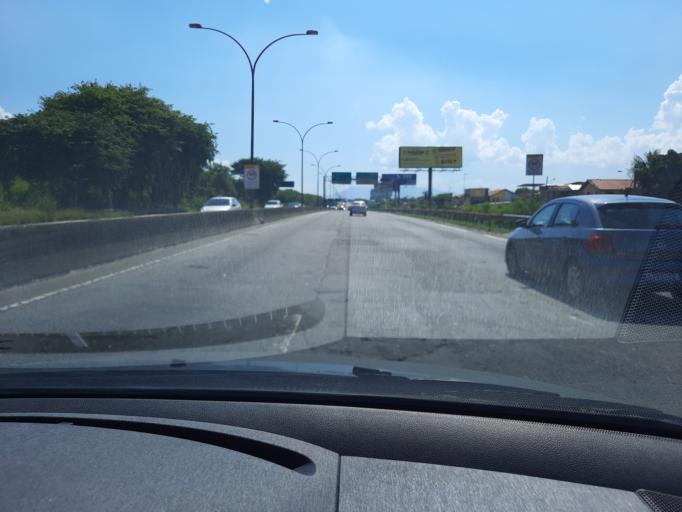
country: BR
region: Rio de Janeiro
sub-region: Duque De Caxias
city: Duque de Caxias
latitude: -22.8085
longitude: -43.2785
